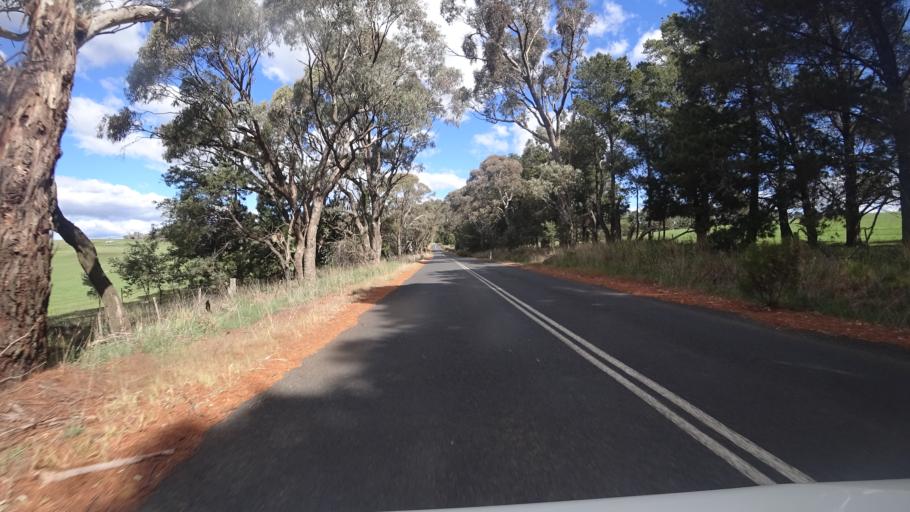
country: AU
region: New South Wales
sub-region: Oberon
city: Oberon
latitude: -33.6771
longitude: 149.7855
